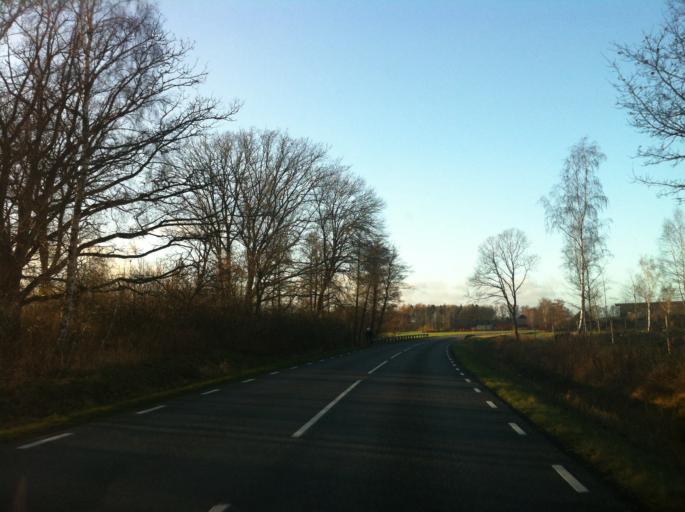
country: SE
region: Skane
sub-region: Ostra Goinge Kommun
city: Knislinge
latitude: 56.1897
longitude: 14.0278
